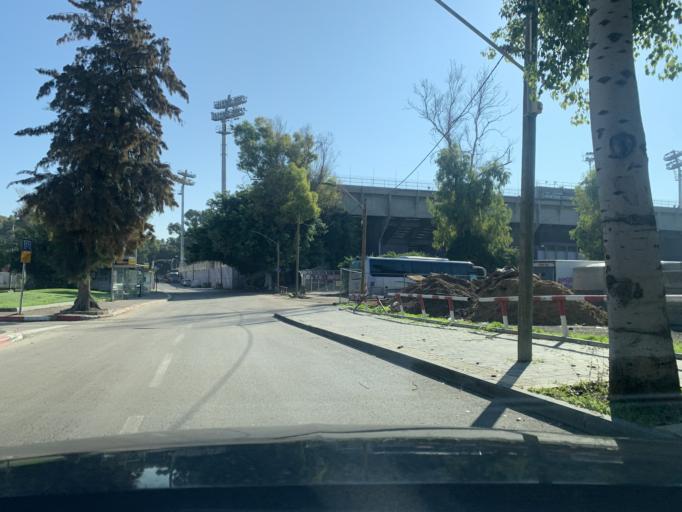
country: IL
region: Tel Aviv
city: Azor
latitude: 32.0463
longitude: 34.8141
